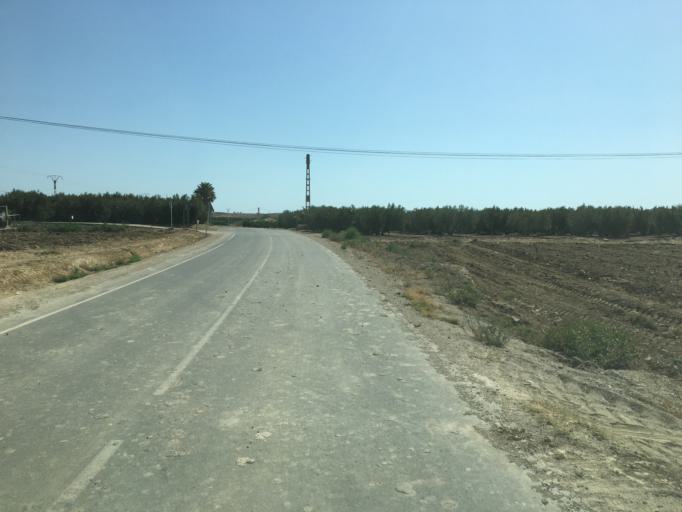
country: ES
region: Andalusia
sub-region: Provincia de Almeria
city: Huercal-Overa
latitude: 37.4214
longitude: -1.8931
